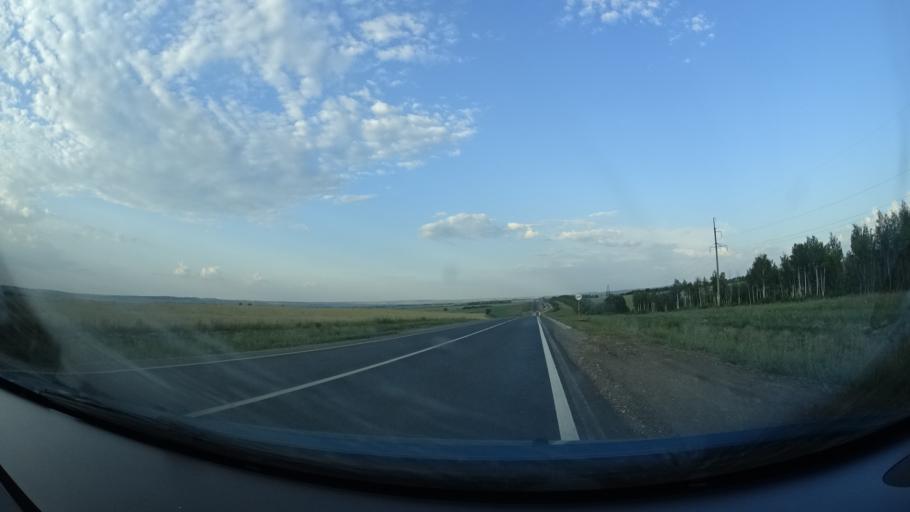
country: RU
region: Samara
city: Kamyshla
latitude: 54.0334
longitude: 51.9279
